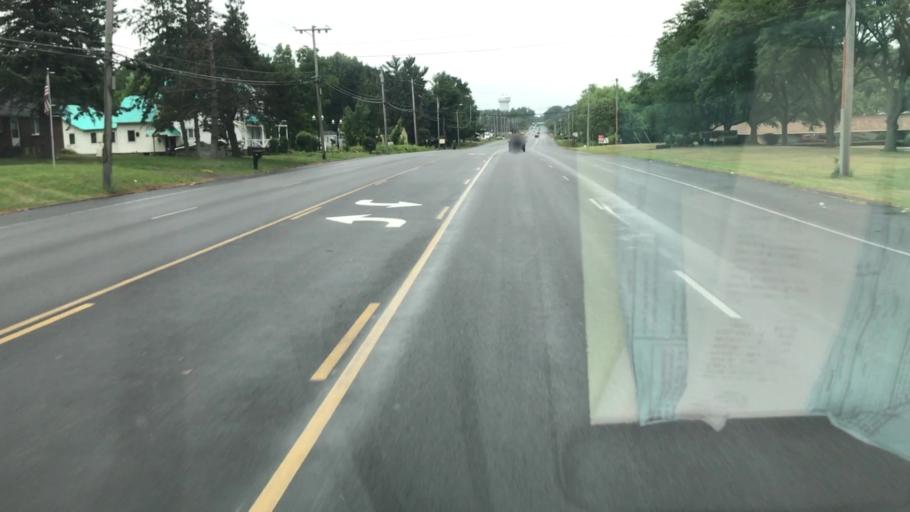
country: US
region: New York
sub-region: Onondaga County
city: Liverpool
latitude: 43.1250
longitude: -76.2174
